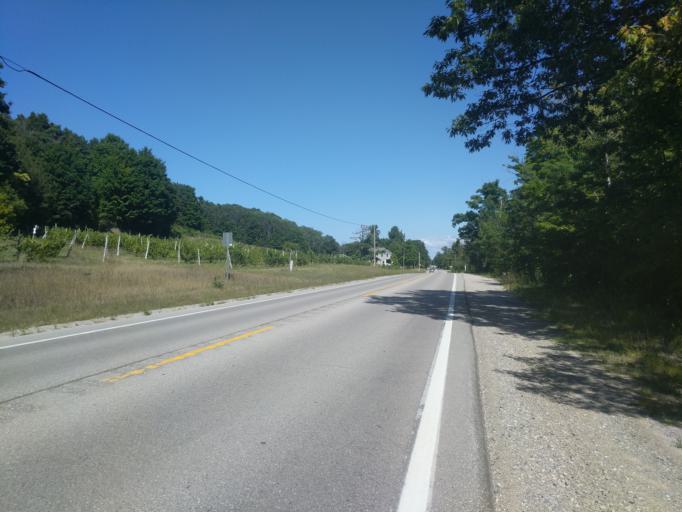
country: US
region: Michigan
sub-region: Leelanau County
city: Leland
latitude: 45.0075
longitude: -85.6220
